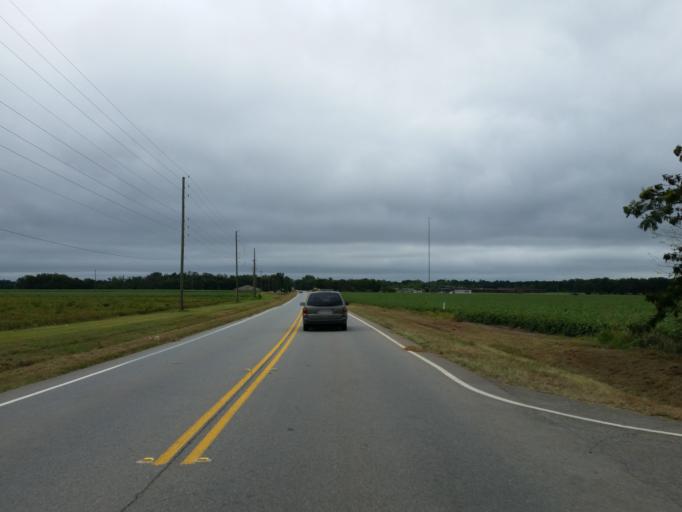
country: US
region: Georgia
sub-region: Peach County
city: Fort Valley
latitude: 32.5796
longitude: -83.9151
